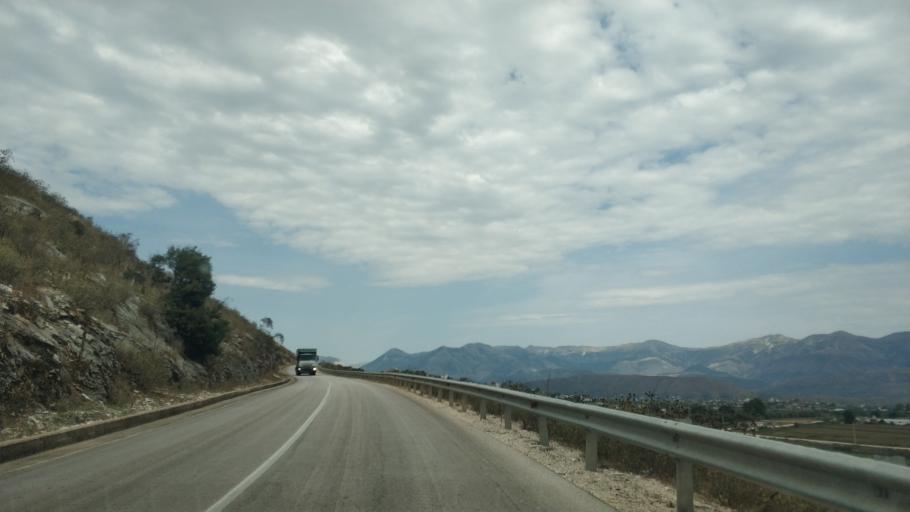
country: AL
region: Vlore
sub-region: Rrethi i Sarandes
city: Sarande
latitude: 39.8586
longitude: 20.0357
